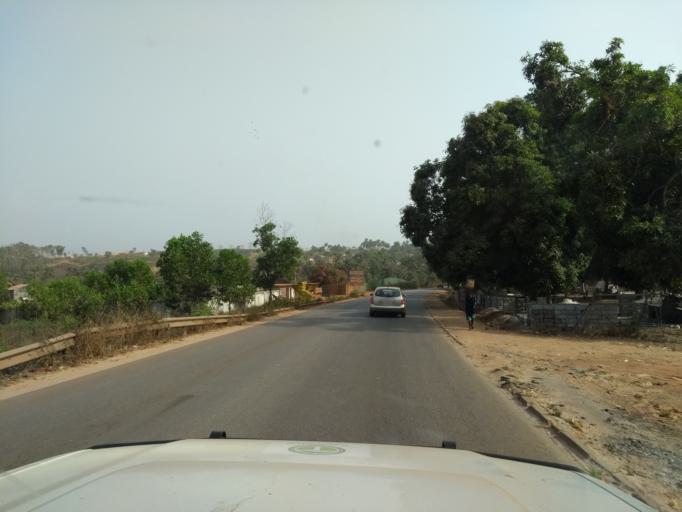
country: GN
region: Kindia
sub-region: Prefecture de Dubreka
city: Dubreka
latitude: 9.8400
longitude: -13.4880
